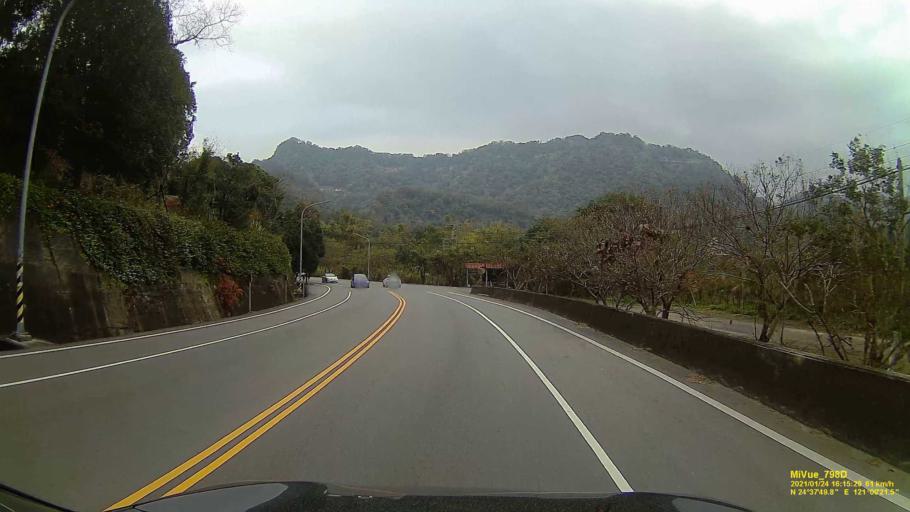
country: TW
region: Taiwan
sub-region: Hsinchu
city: Hsinchu
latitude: 24.6308
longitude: 121.0060
